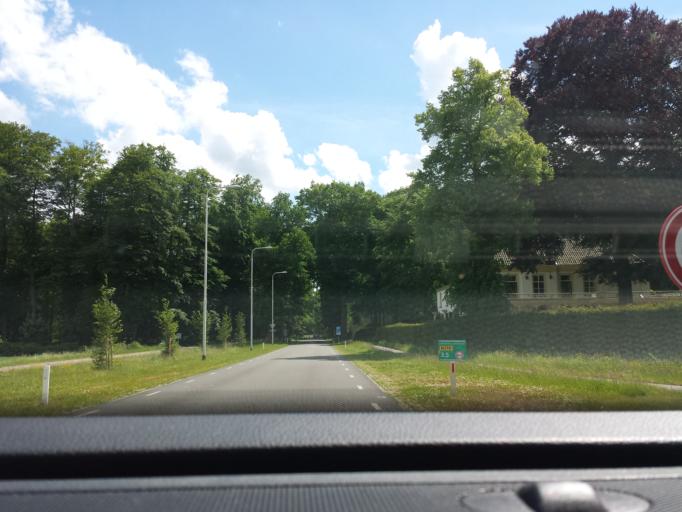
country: NL
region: Gelderland
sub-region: Gemeente Zutphen
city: Warnsveld
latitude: 52.1429
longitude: 6.2442
